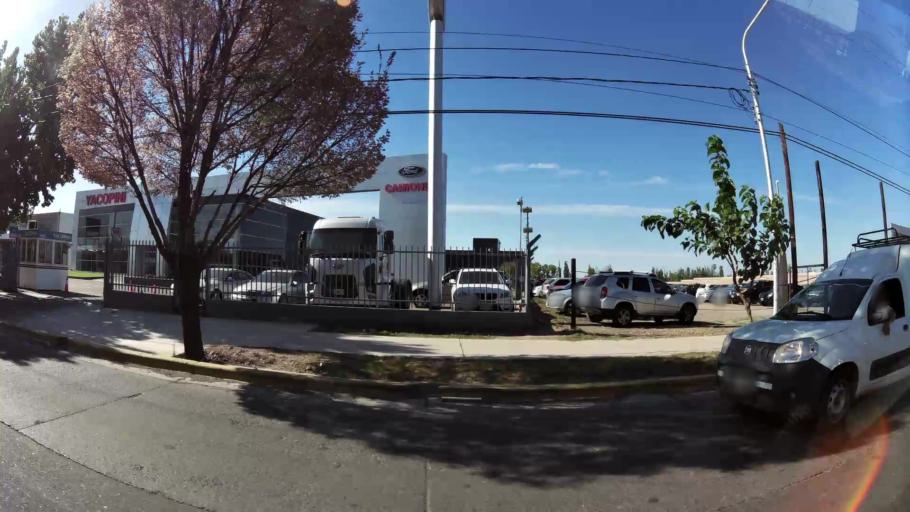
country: AR
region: Mendoza
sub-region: Departamento de Godoy Cruz
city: Godoy Cruz
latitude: -32.9278
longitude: -68.8173
